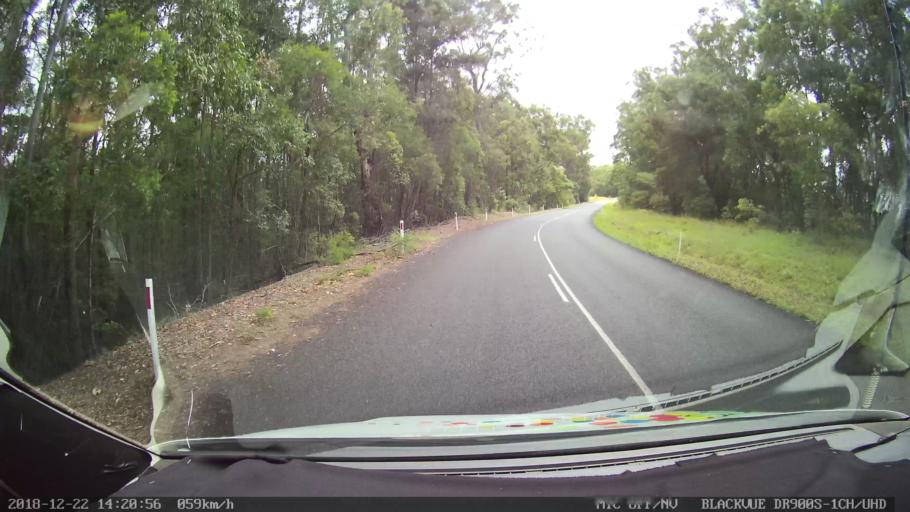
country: AU
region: New South Wales
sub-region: Clarence Valley
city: Coutts Crossing
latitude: -30.0185
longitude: 152.6635
